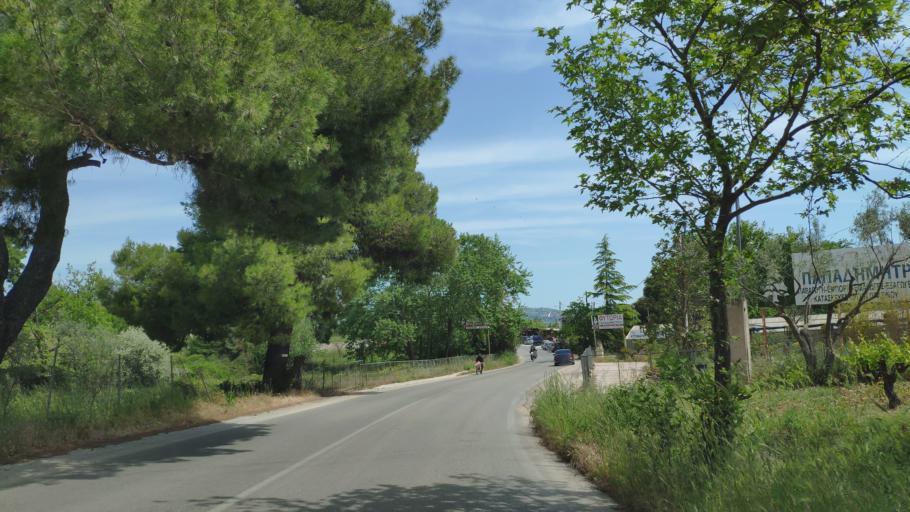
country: GR
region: Attica
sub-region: Nomarchia Anatolikis Attikis
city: Agios Stefanos
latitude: 38.1673
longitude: 23.8614
